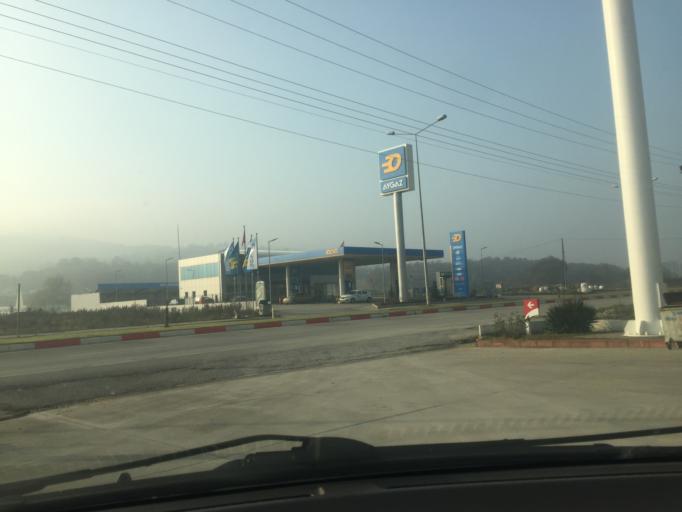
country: TR
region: Canakkale
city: Can
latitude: 40.0379
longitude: 27.0757
